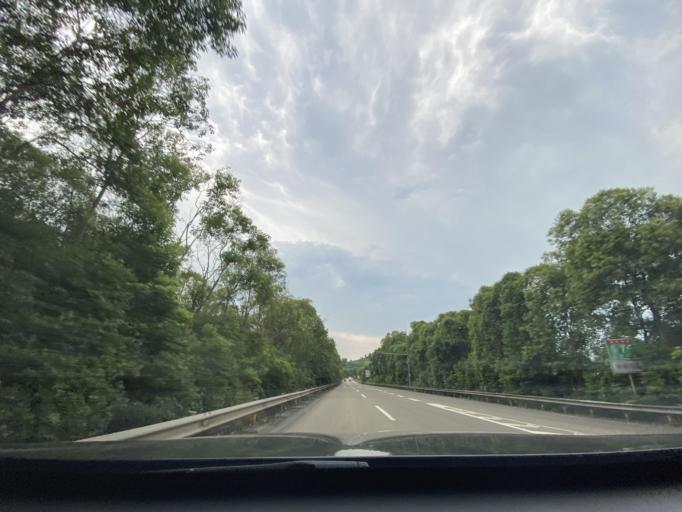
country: CN
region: Sichuan
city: Chonglong
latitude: 29.6865
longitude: 104.9515
